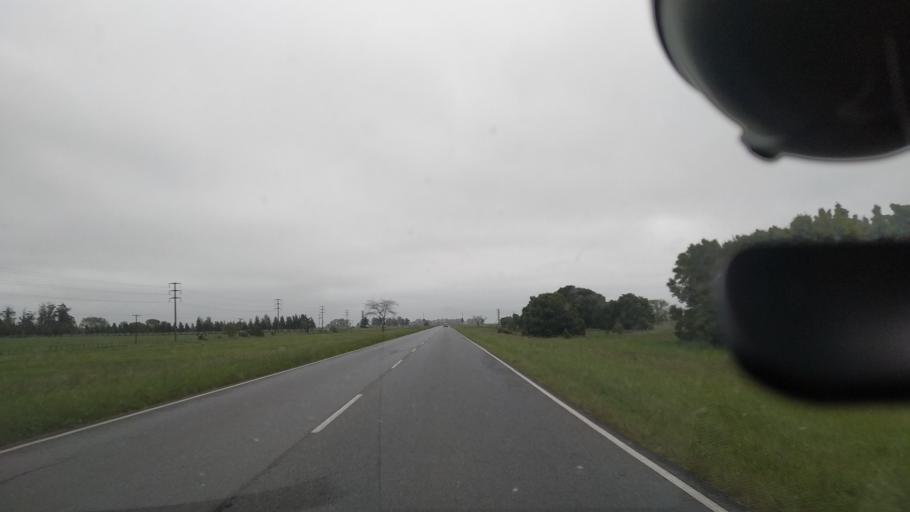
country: AR
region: Buenos Aires
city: Veronica
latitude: -35.3498
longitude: -57.4323
